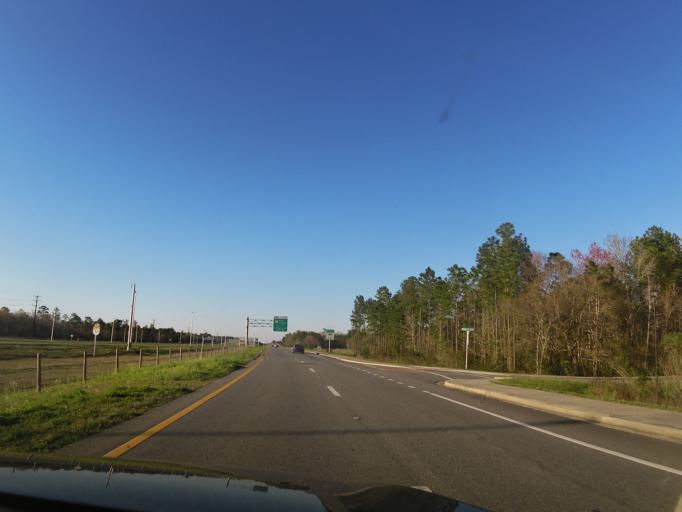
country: US
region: Florida
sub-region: Clay County
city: Middleburg
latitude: 30.1195
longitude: -81.8298
